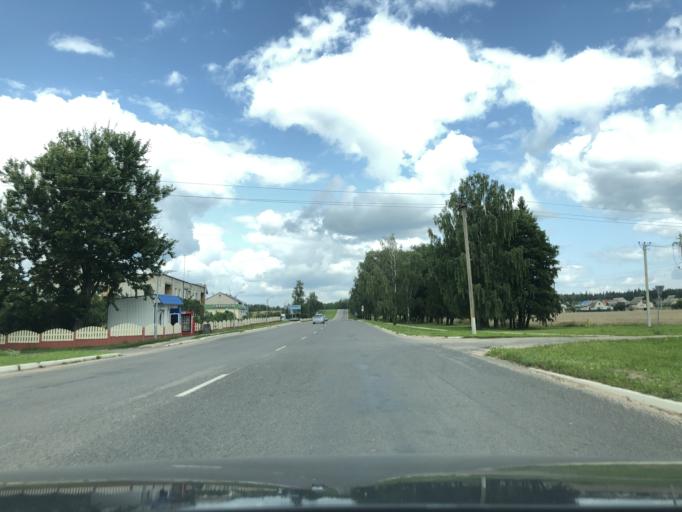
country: BY
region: Minsk
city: Lahoysk
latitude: 54.2193
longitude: 27.8512
